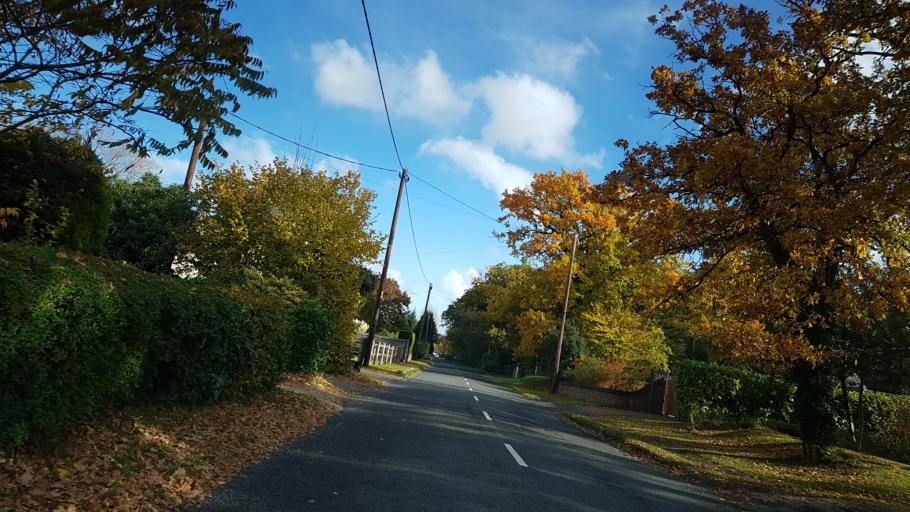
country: GB
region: England
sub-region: Surrey
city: Seale
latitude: 51.2214
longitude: -0.7392
